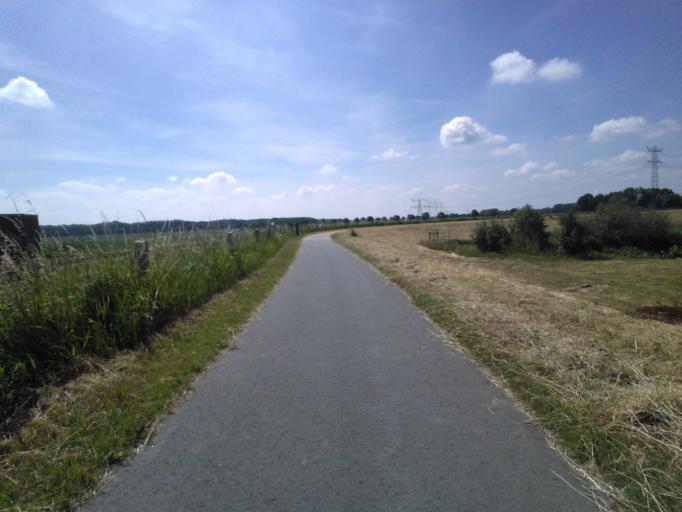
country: NL
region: North Brabant
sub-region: Gemeente Werkendam
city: Werkendam
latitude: 51.7652
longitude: 4.8643
